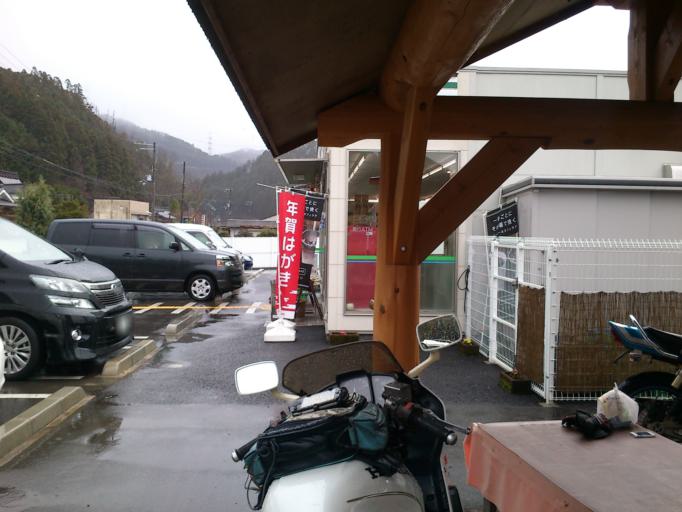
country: JP
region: Kyoto
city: Kameoka
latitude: 35.1512
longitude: 135.6345
